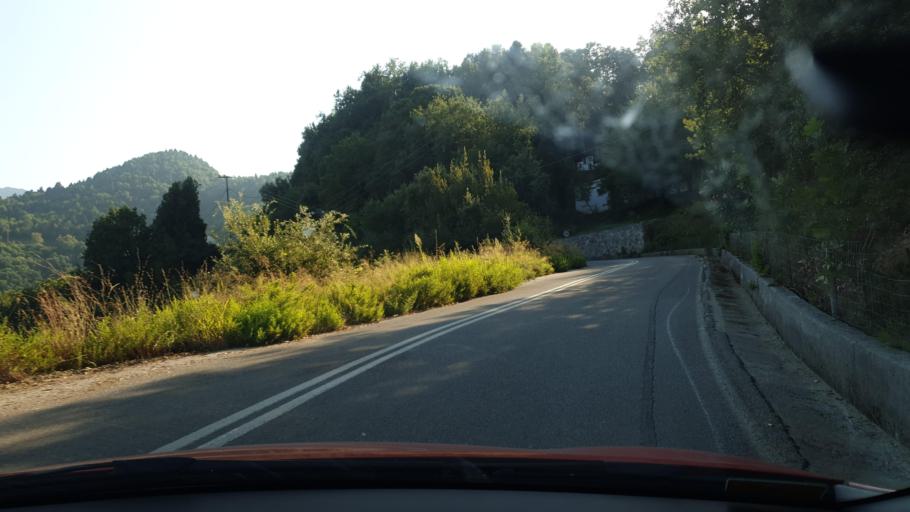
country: GR
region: Central Greece
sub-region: Nomos Evvoias
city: Kymi
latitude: 38.6432
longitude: 23.9386
